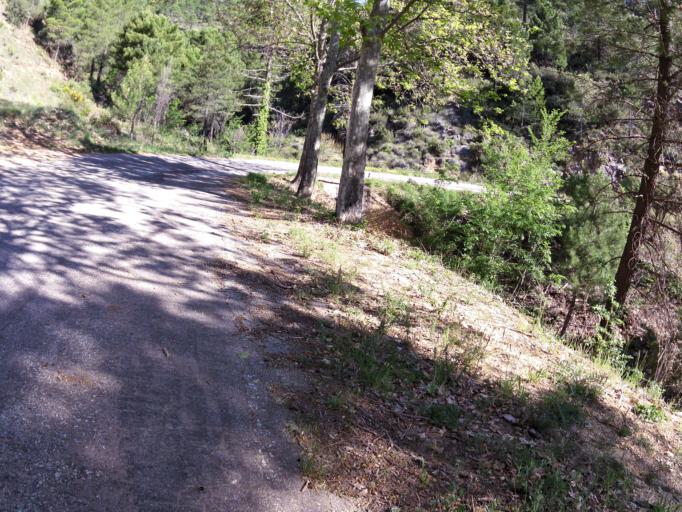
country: ES
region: Castille-La Mancha
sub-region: Provincia de Albacete
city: Riopar
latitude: 38.5238
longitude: -2.4561
